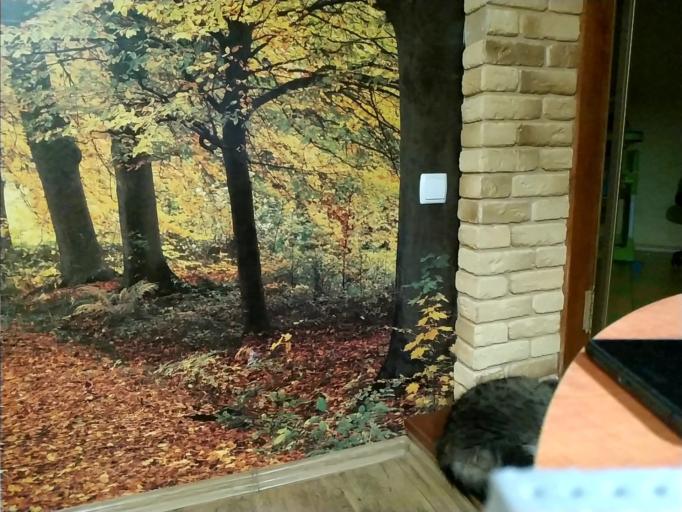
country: RU
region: Tverskaya
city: Zubtsov
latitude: 56.2753
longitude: 34.6925
